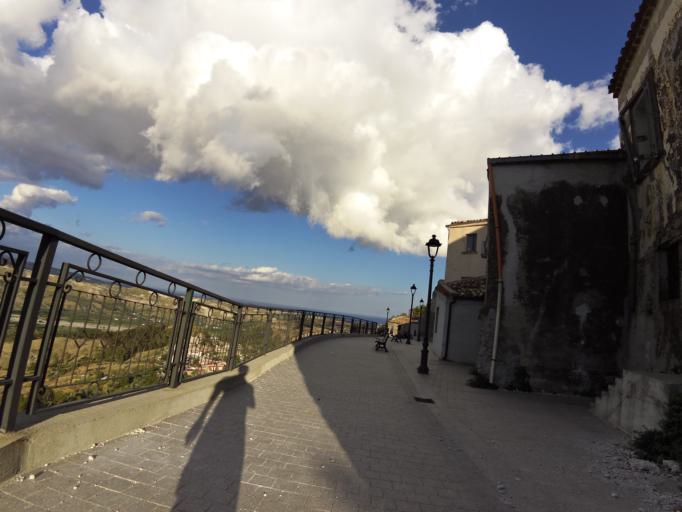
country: IT
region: Calabria
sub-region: Provincia di Reggio Calabria
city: Caulonia
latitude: 38.3832
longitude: 16.4069
